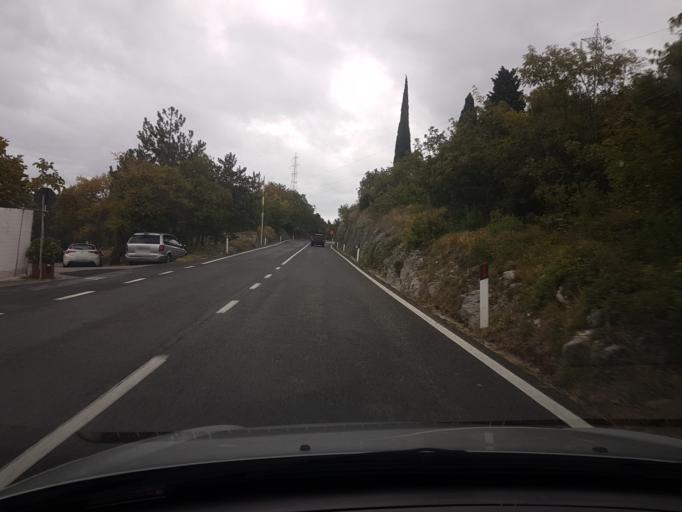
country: IT
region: Friuli Venezia Giulia
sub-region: Provincia di Trieste
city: Duino
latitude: 45.8065
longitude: 13.5814
